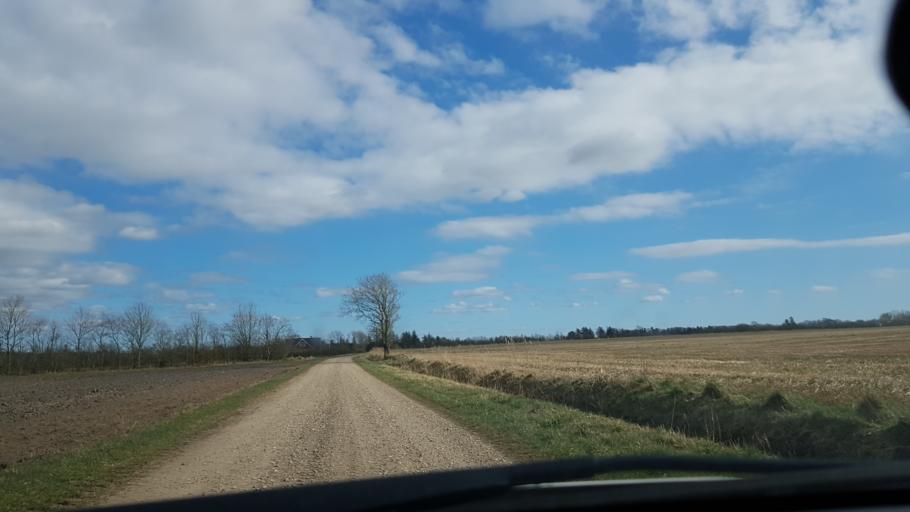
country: DK
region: South Denmark
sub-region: Esbjerg Kommune
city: Ribe
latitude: 55.2867
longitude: 8.8105
